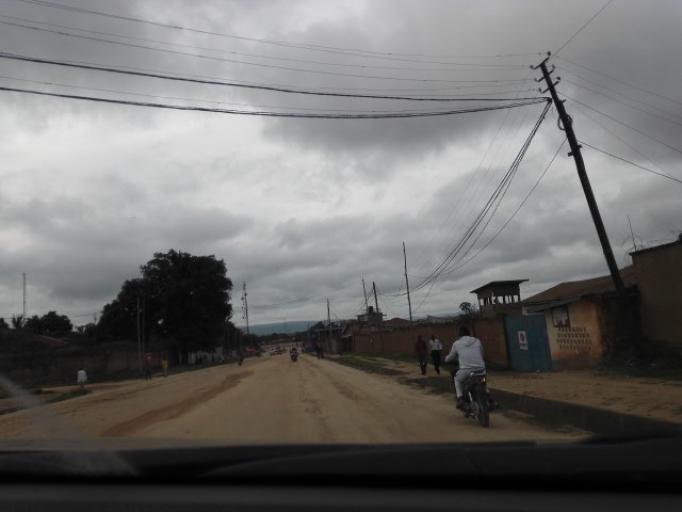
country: CD
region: Eastern Province
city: Bunia
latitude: 1.5484
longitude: 30.2490
